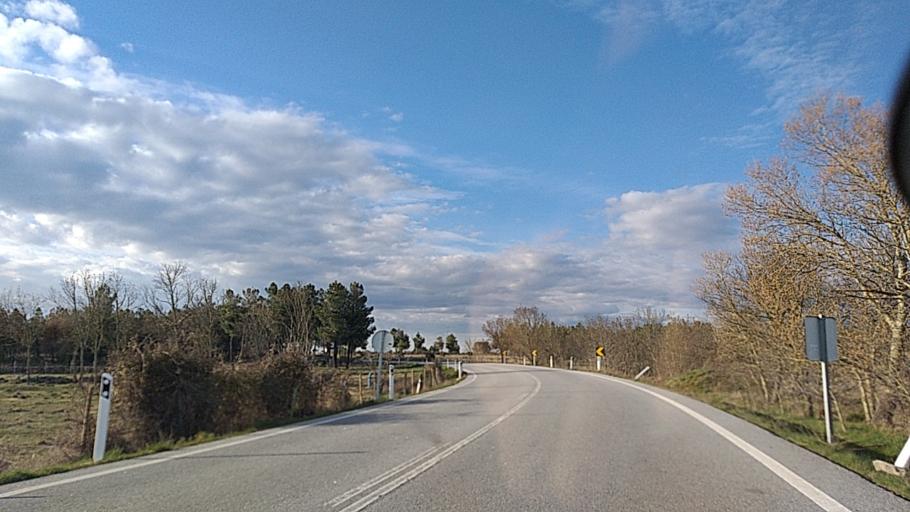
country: ES
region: Castille and Leon
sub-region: Provincia de Salamanca
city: Aldea del Obispo
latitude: 40.6693
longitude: -6.8591
